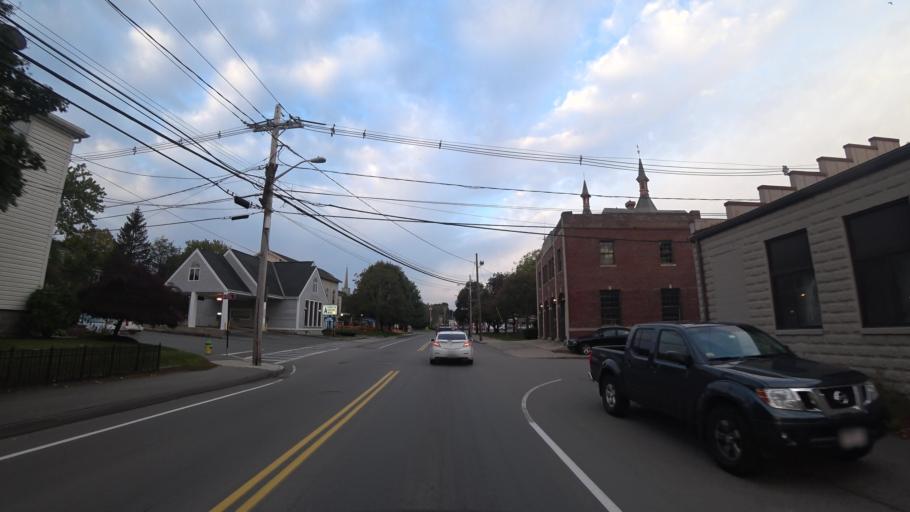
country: US
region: Massachusetts
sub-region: Essex County
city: Saugus
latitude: 42.4651
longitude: -71.0082
